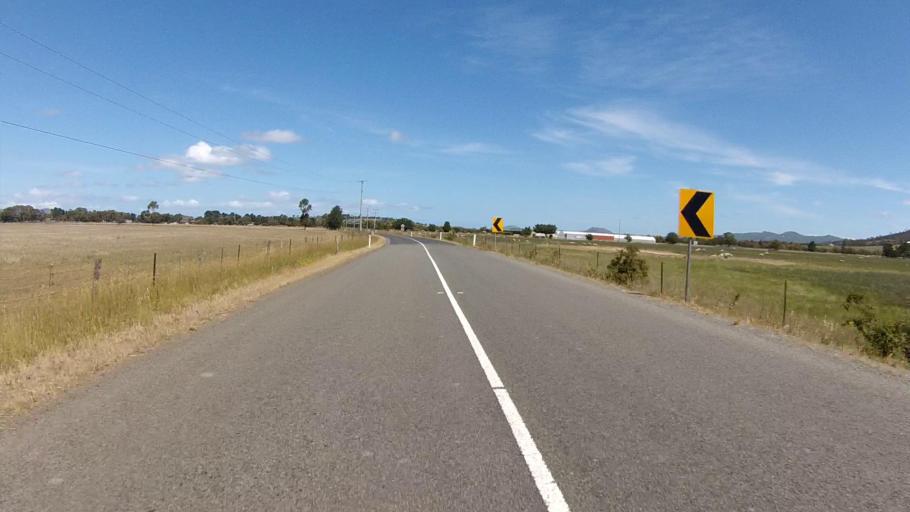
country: AU
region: Tasmania
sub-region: Sorell
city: Sorell
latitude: -42.7686
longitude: 147.5173
